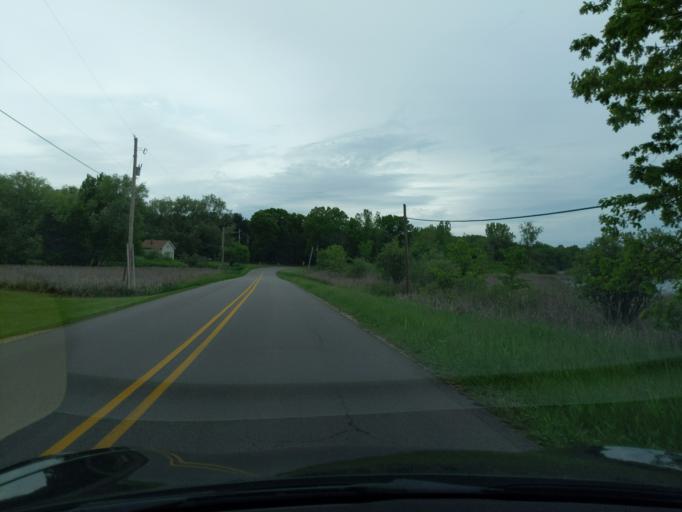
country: US
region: Michigan
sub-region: Jackson County
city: Jackson
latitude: 42.3549
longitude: -84.3489
